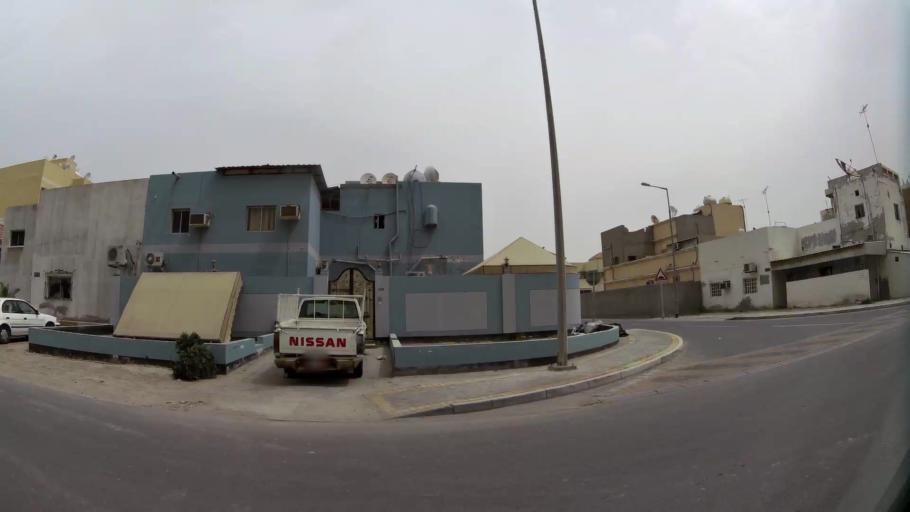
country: BH
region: Northern
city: Madinat `Isa
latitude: 26.1767
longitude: 50.5415
